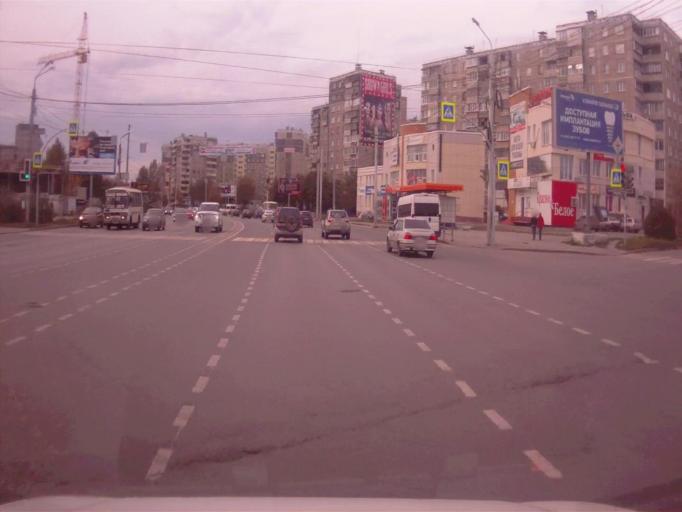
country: RU
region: Chelyabinsk
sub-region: Gorod Chelyabinsk
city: Chelyabinsk
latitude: 55.1782
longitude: 61.3721
